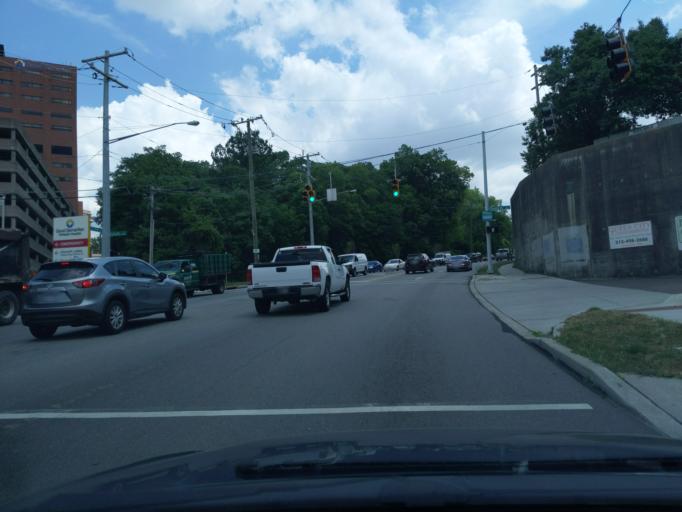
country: US
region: Ohio
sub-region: Hamilton County
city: Saint Bernard
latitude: 39.1396
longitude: -84.5246
